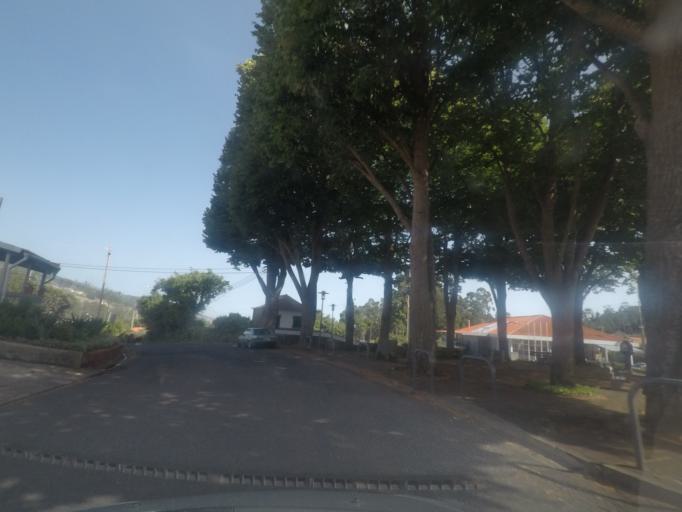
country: PT
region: Madeira
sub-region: Calheta
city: Estreito da Calheta
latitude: 32.7548
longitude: -17.2013
